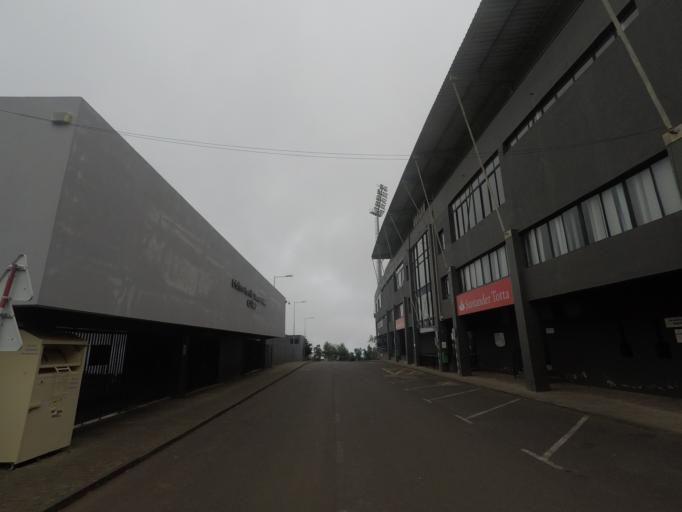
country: PT
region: Madeira
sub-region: Funchal
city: Nossa Senhora do Monte
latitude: 32.6710
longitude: -16.8829
